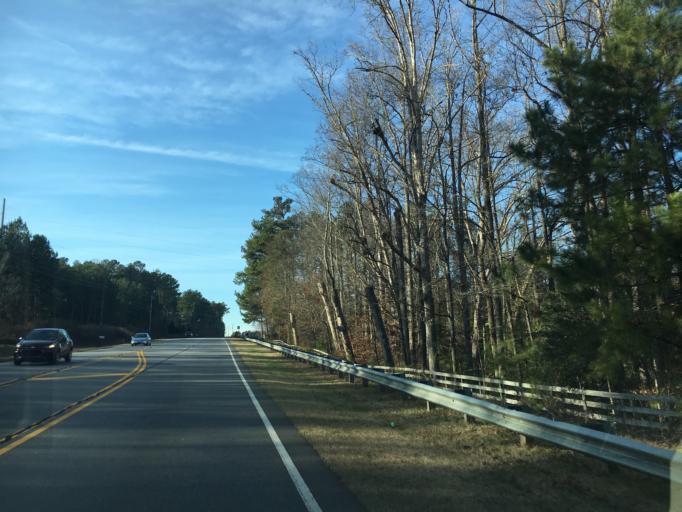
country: US
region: Georgia
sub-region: Hart County
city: Hartwell
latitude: 34.3647
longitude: -82.9774
